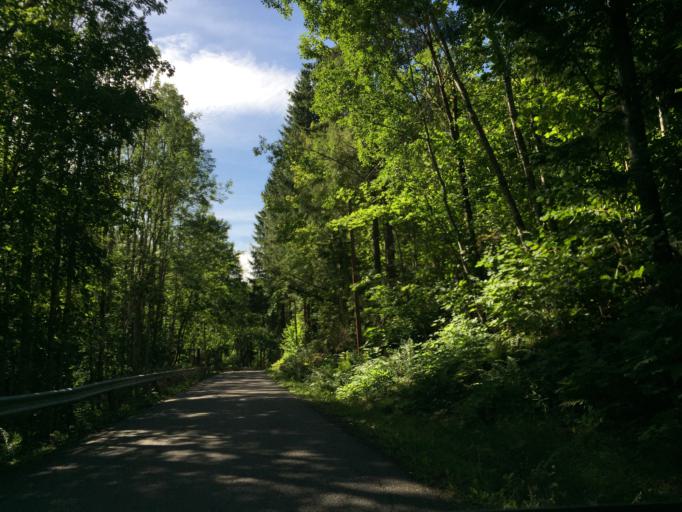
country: NO
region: Vestfold
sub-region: Hof
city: Hof
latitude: 59.4818
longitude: 10.1501
